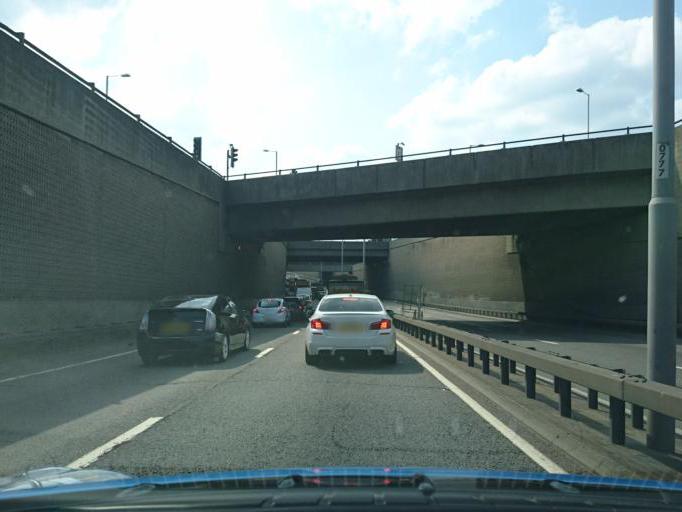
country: GB
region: England
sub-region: Greater London
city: Enfield
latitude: 51.6161
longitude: -0.0843
